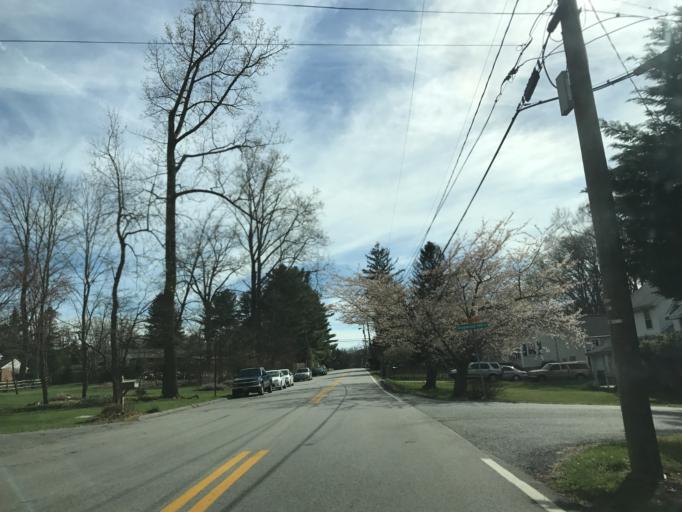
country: US
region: Maryland
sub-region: Baltimore County
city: Hampton
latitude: 39.4333
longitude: -76.5560
